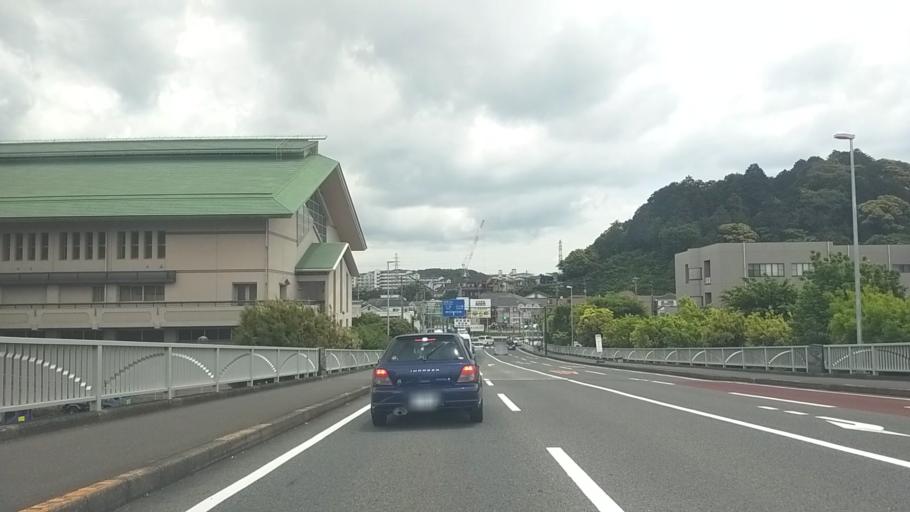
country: JP
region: Kanagawa
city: Kamakura
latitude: 35.3462
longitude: 139.5237
